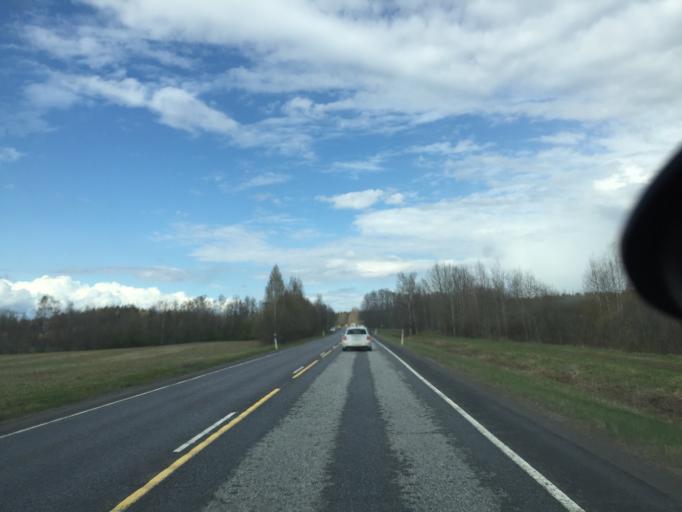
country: FI
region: Uusimaa
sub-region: Helsinki
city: Lohja
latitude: 60.2037
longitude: 24.0192
